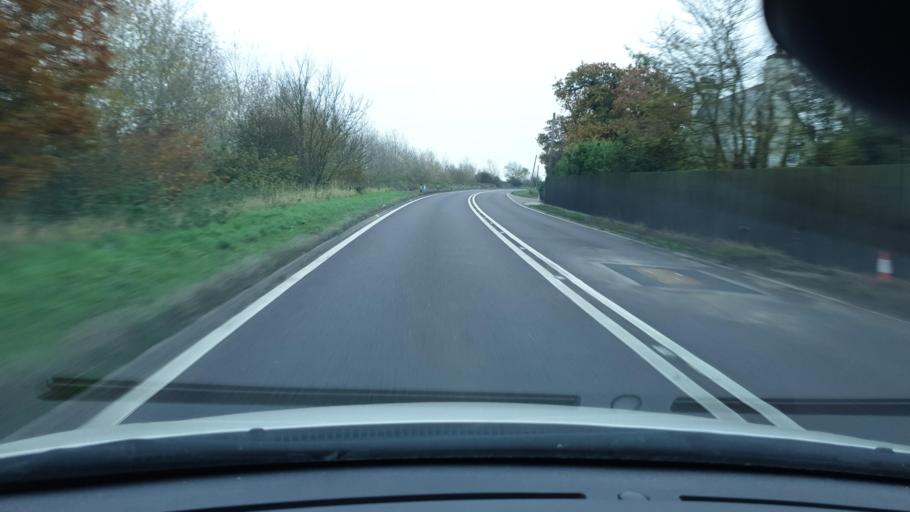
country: GB
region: England
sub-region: Suffolk
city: Shotley Gate
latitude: 51.9245
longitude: 1.1824
